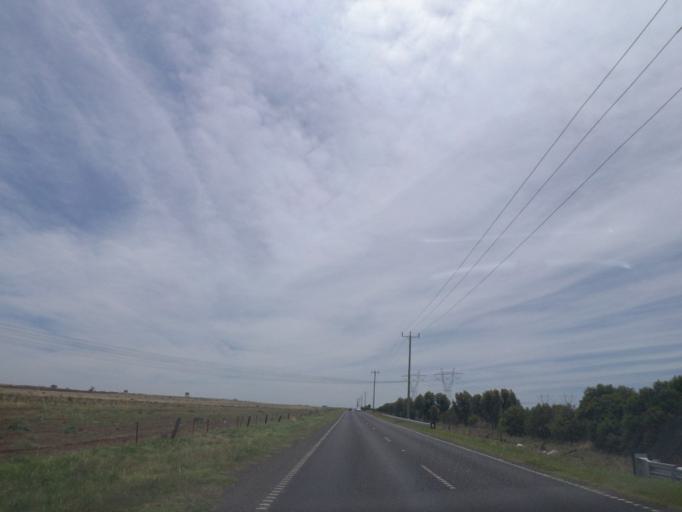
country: AU
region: Victoria
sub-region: Melton
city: Caroline Springs
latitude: -37.7675
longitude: 144.7015
